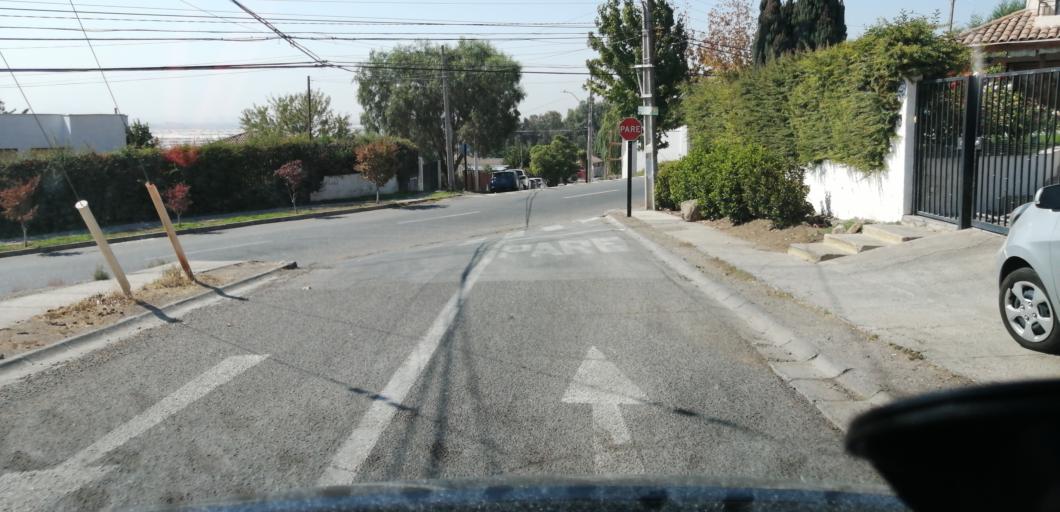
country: CL
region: Santiago Metropolitan
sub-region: Provincia de Santiago
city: Lo Prado
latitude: -33.4569
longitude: -70.8214
